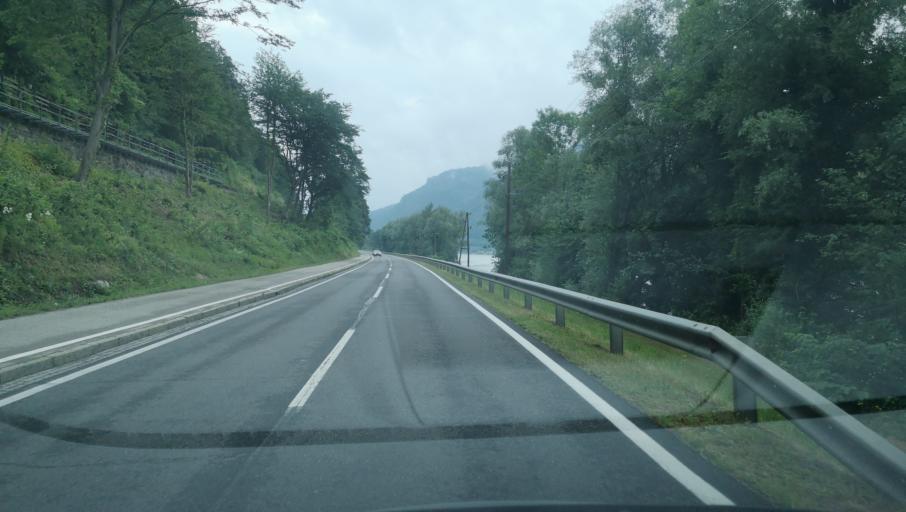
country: AT
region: Lower Austria
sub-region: Politischer Bezirk Krems
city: Aggsbach
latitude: 48.3031
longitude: 15.4064
